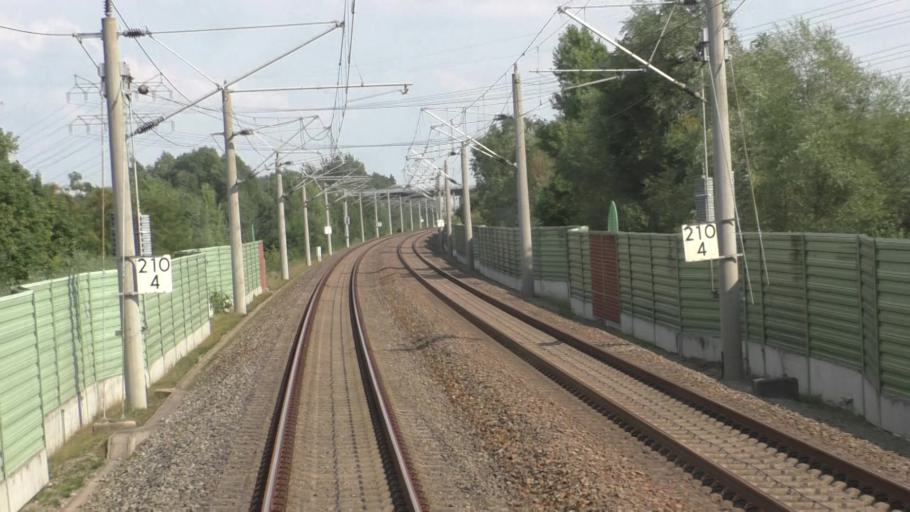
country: DE
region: Saxony-Anhalt
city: Uenglingen
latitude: 52.5802
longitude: 11.7873
